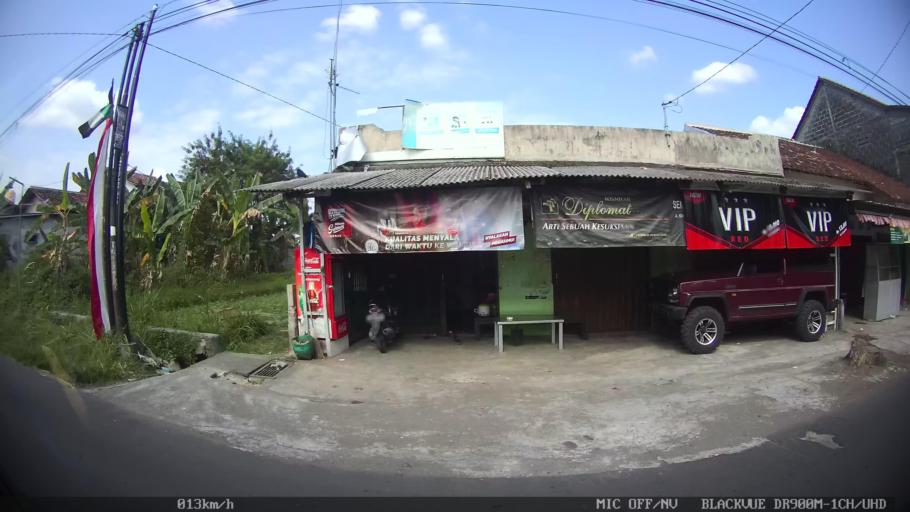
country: ID
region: Daerah Istimewa Yogyakarta
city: Depok
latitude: -7.7291
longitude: 110.4140
